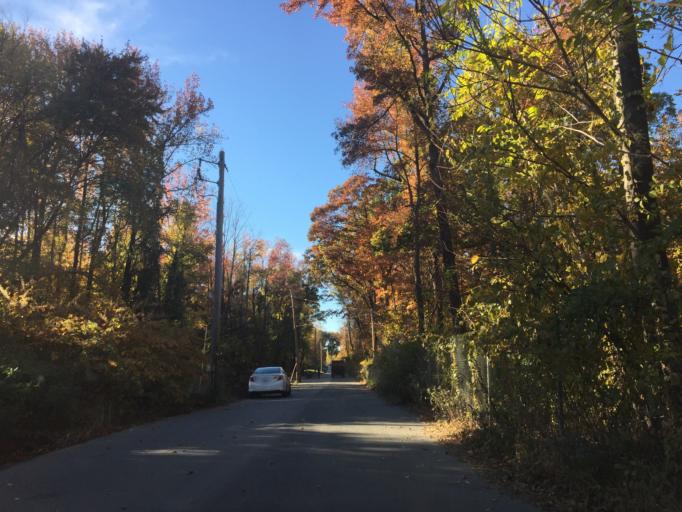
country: US
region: Maryland
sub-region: Baltimore County
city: Rosedale
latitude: 39.3182
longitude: -76.5002
